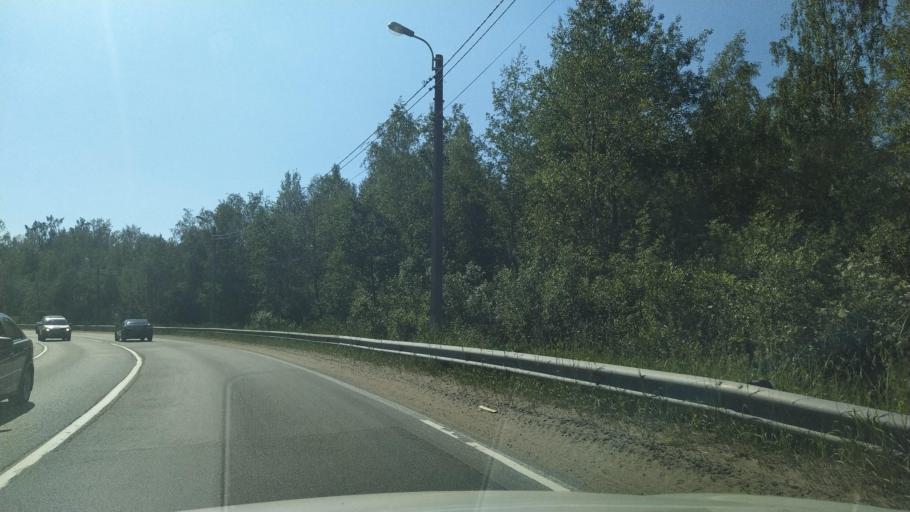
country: RU
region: St.-Petersburg
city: Beloostrov
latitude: 60.1467
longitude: 29.9931
